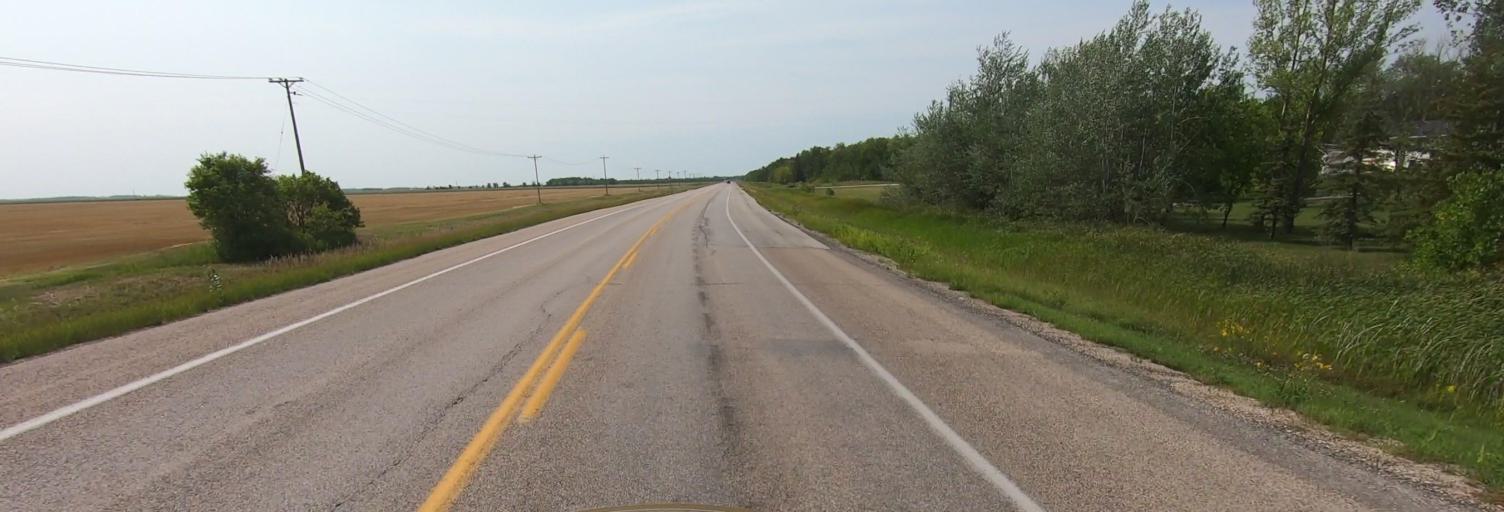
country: CA
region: Manitoba
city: Niverville
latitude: 49.6554
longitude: -97.1013
